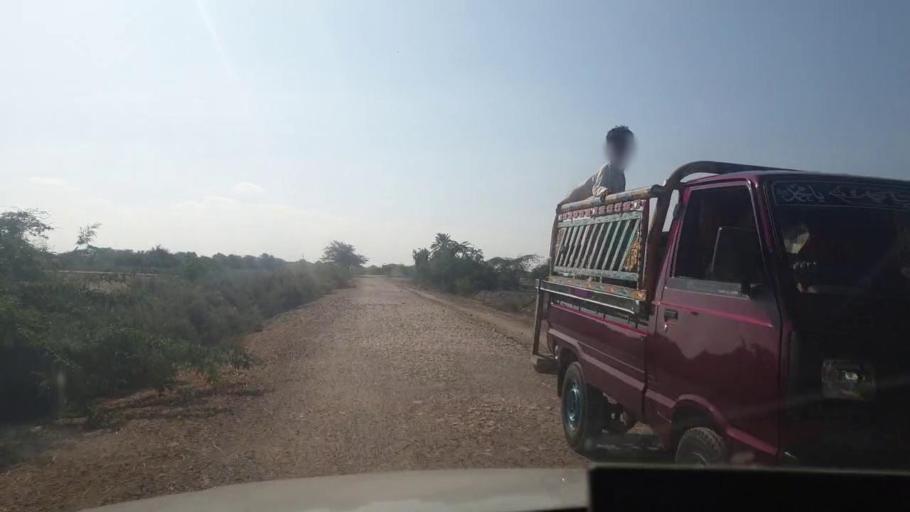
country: PK
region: Sindh
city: Mirpur Sakro
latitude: 24.4718
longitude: 67.5956
